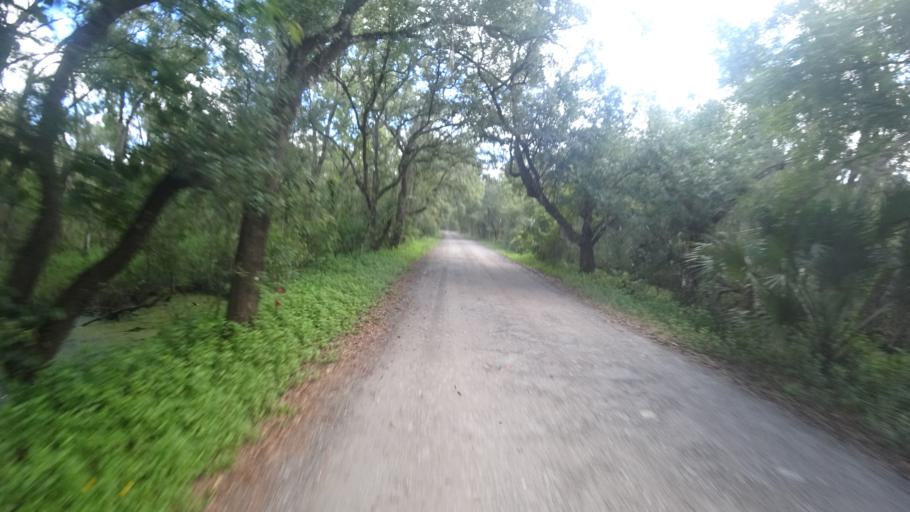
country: US
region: Florida
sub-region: Sarasota County
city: Lake Sarasota
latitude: 27.3275
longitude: -82.2687
